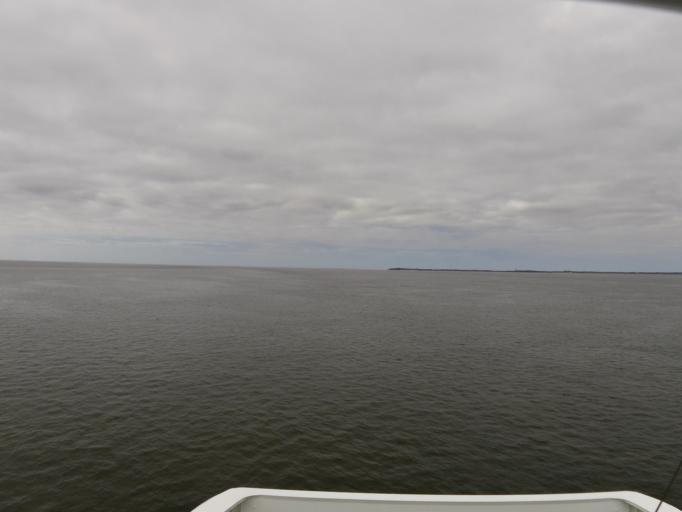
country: DE
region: Schleswig-Holstein
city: Nieblum
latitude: 54.6497
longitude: 8.4709
